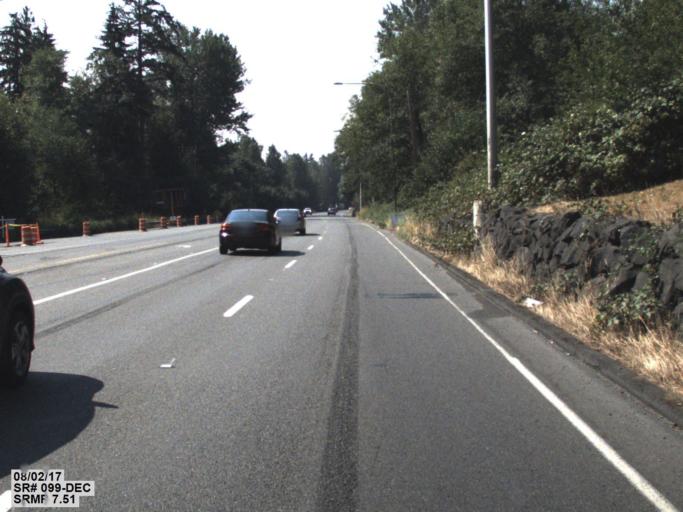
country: US
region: Washington
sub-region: Pierce County
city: Fife Heights
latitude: 47.2810
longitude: -122.3230
